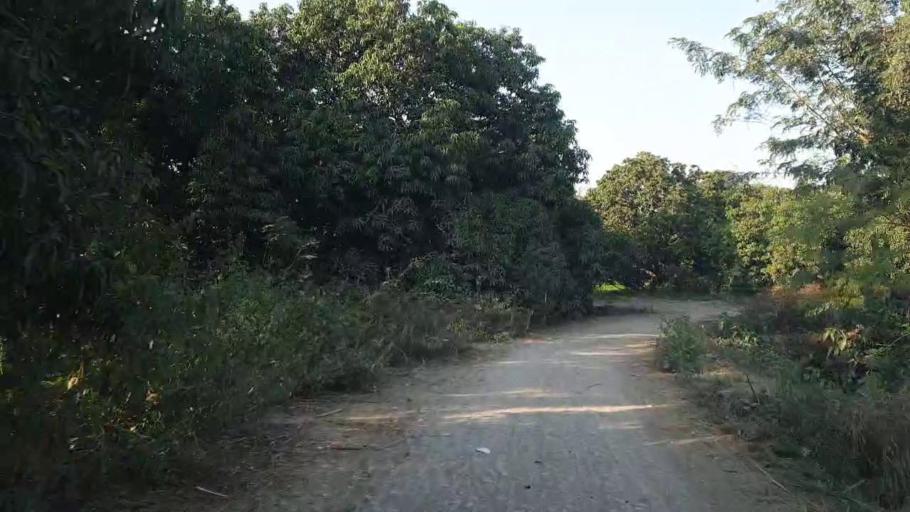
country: PK
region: Sindh
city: Mirpur Khas
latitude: 25.4399
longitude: 68.9106
